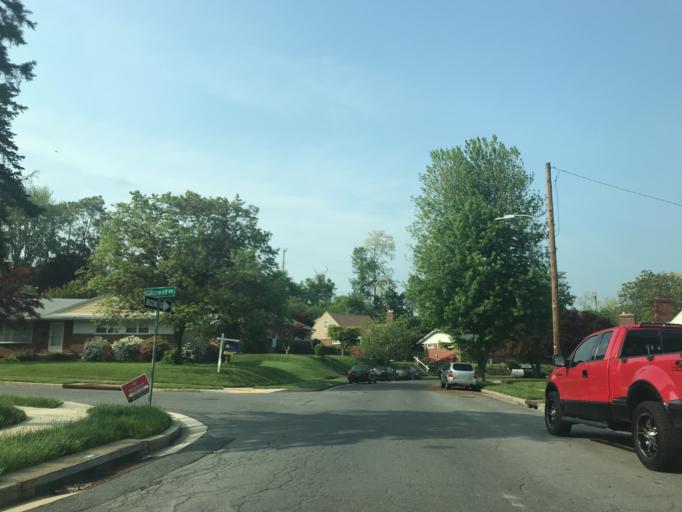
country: US
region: Maryland
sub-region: Baltimore County
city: Towson
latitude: 39.3817
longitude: -76.5764
